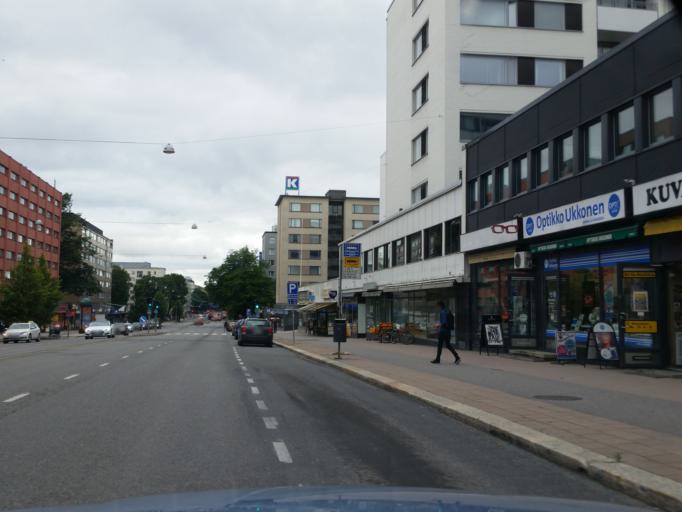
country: FI
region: Varsinais-Suomi
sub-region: Turku
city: Turku
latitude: 60.4532
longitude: 22.2860
